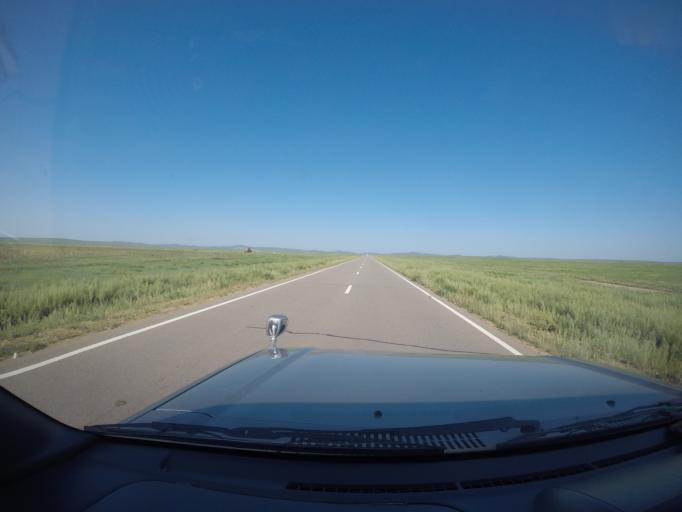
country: MN
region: Suhbaatar
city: Hanhohiy
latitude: 47.5684
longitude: 112.2602
